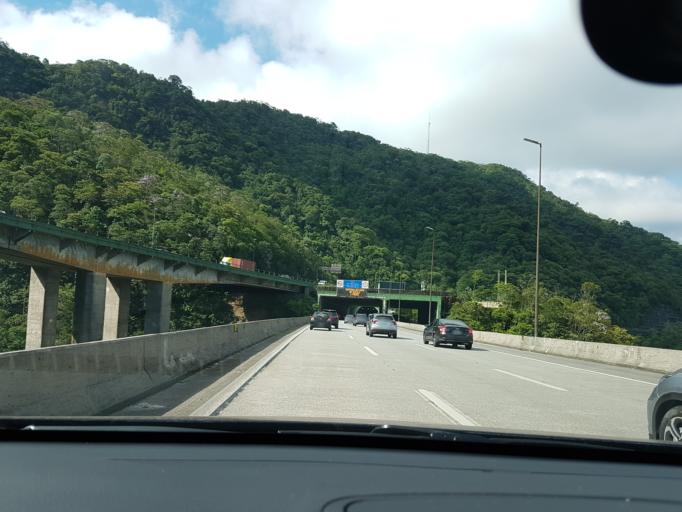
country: BR
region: Sao Paulo
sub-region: Cubatao
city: Cubatao
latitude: -23.9203
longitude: -46.5313
